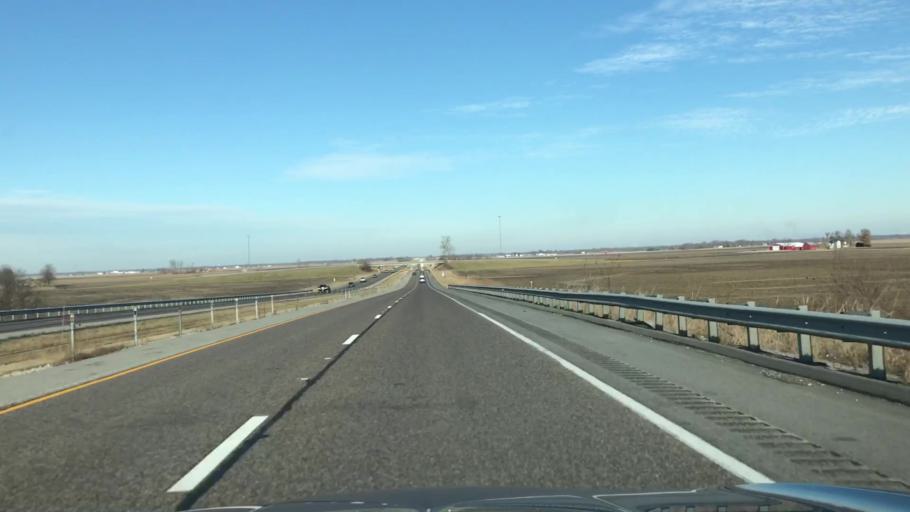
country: US
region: Illinois
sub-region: Madison County
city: Edwardsville
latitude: 38.8266
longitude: -89.8818
